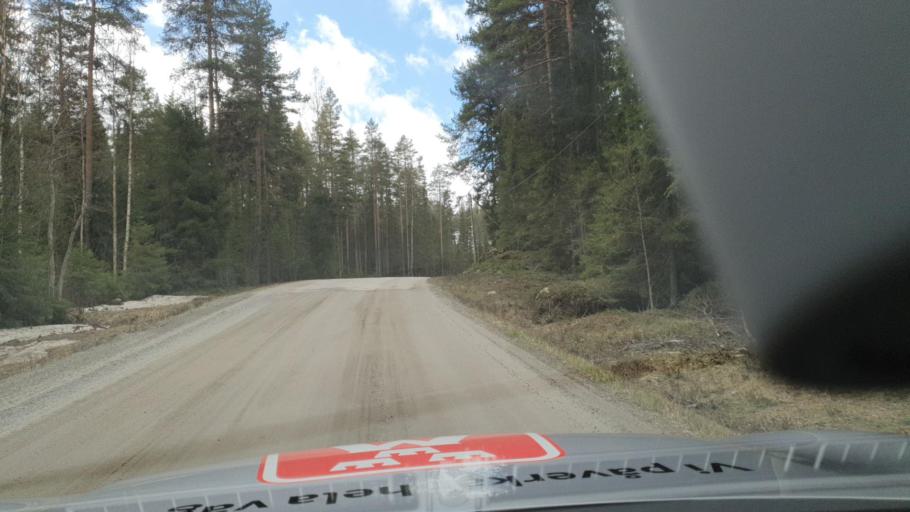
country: SE
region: Vaesterbotten
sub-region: Bjurholms Kommun
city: Bjurholm
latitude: 63.6983
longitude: 18.8963
